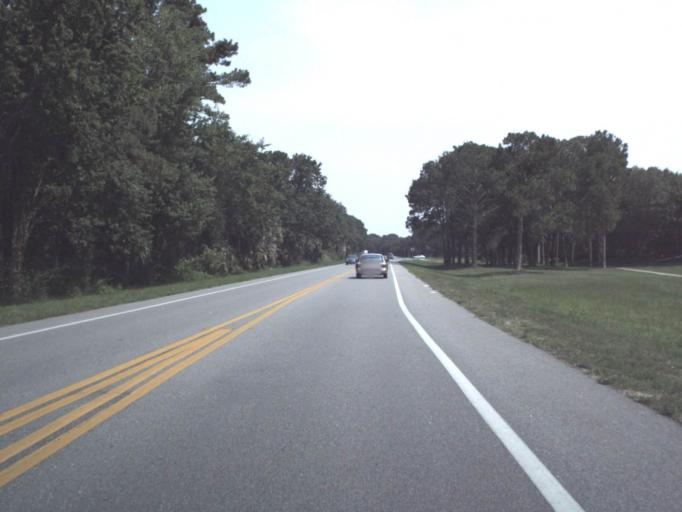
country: US
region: Florida
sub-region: Saint Johns County
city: Palm Valley
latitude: 30.1770
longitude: -81.3763
